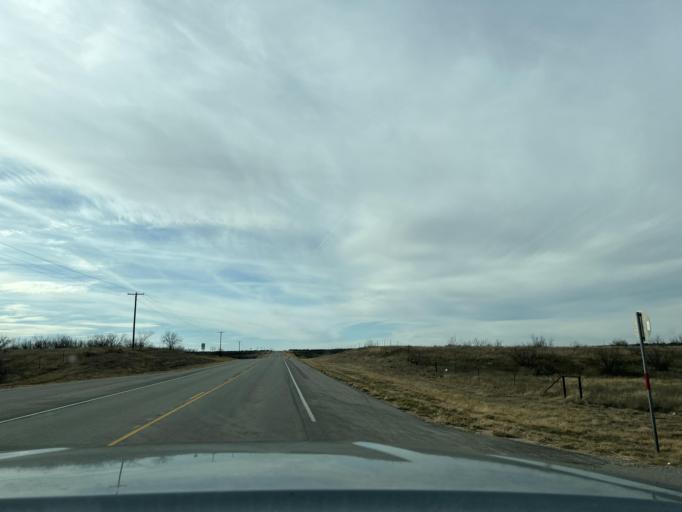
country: US
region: Texas
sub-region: Jones County
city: Anson
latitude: 32.7504
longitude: -99.6528
